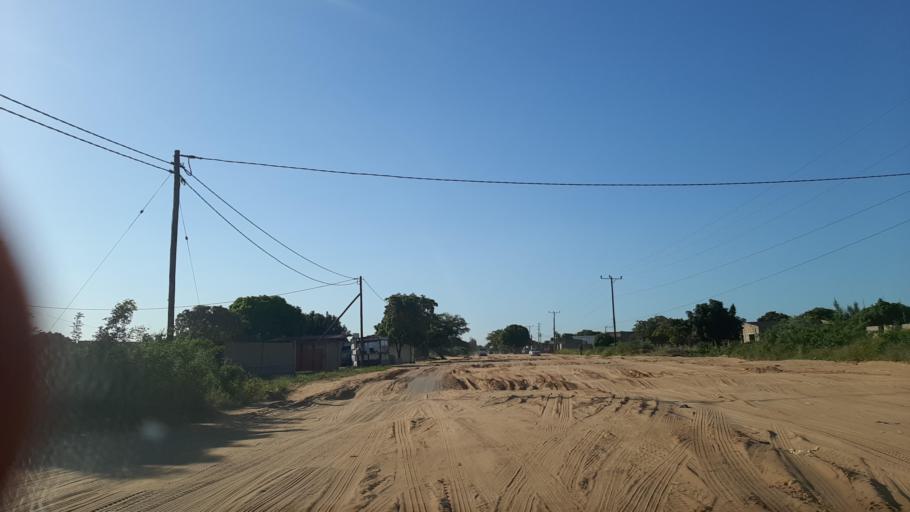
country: MZ
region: Maputo City
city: Maputo
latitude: -25.7488
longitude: 32.5460
